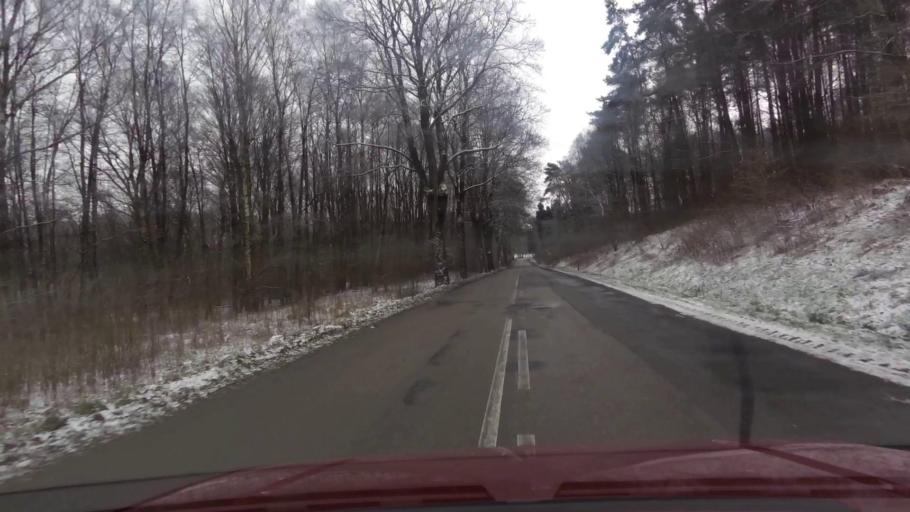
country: PL
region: West Pomeranian Voivodeship
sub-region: Powiat swidwinski
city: Polczyn-Zdroj
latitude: 53.7962
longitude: 16.0573
